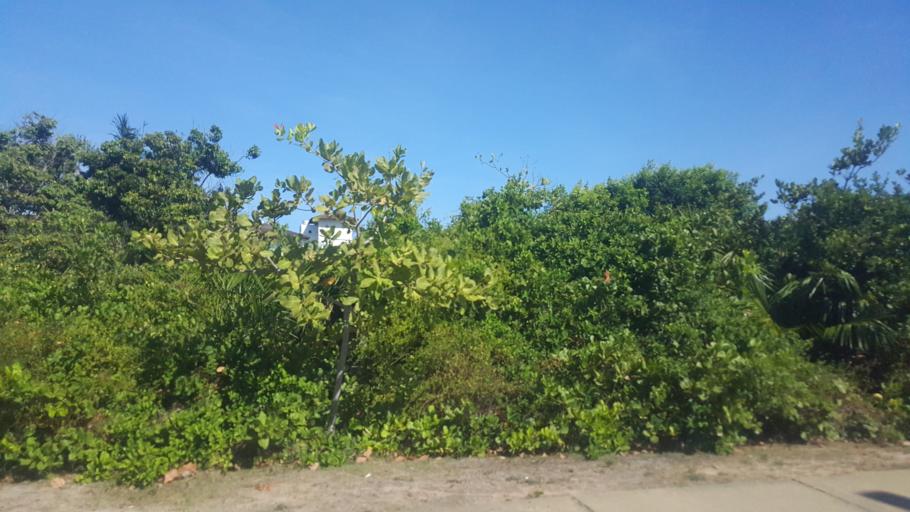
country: BR
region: Bahia
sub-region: Mata De Sao Joao
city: Mata de Sao Joao
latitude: -12.4415
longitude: -37.9236
